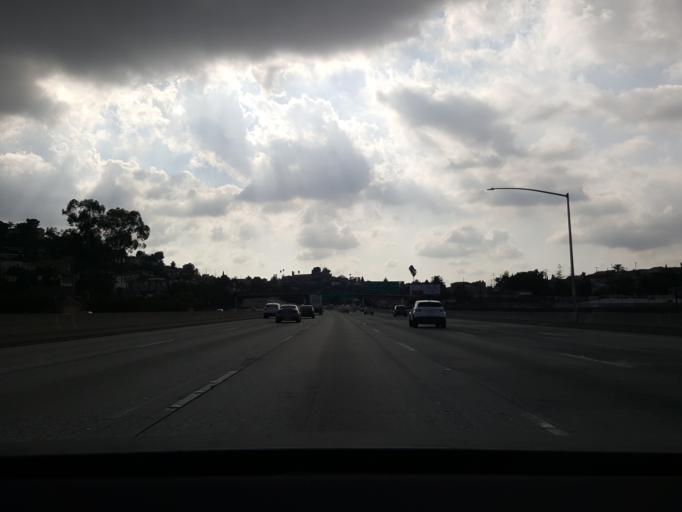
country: US
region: California
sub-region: Los Angeles County
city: Belvedere
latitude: 34.0582
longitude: -118.1793
